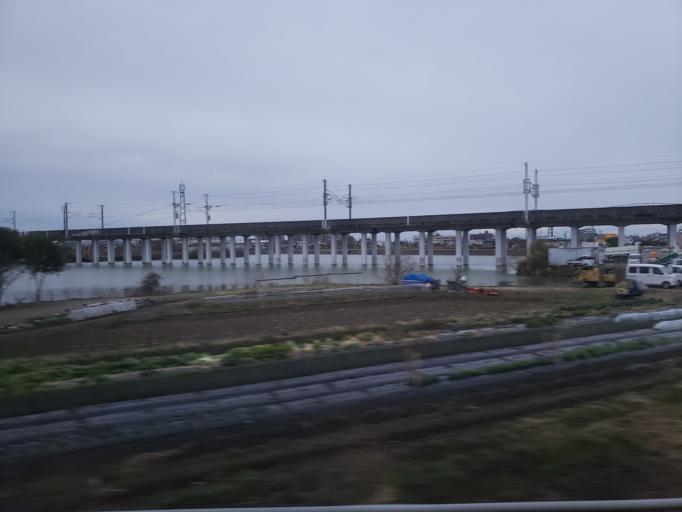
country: JP
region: Hyogo
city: Akashi
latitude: 34.6915
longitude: 134.9130
